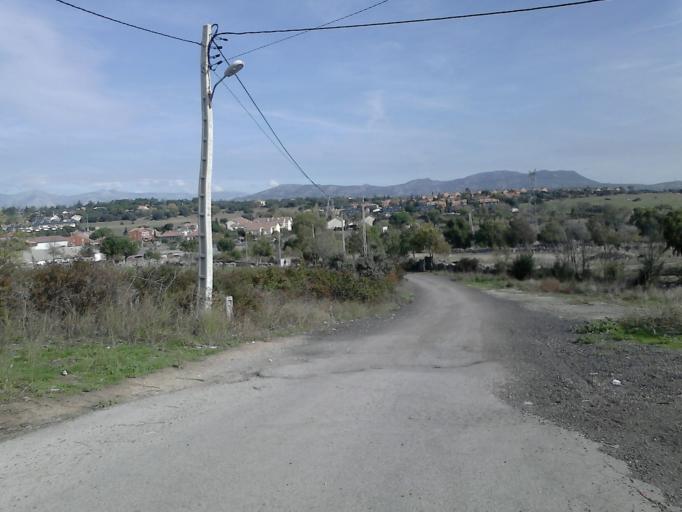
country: ES
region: Madrid
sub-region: Provincia de Madrid
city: Galapagar
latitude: 40.5777
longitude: -3.9956
